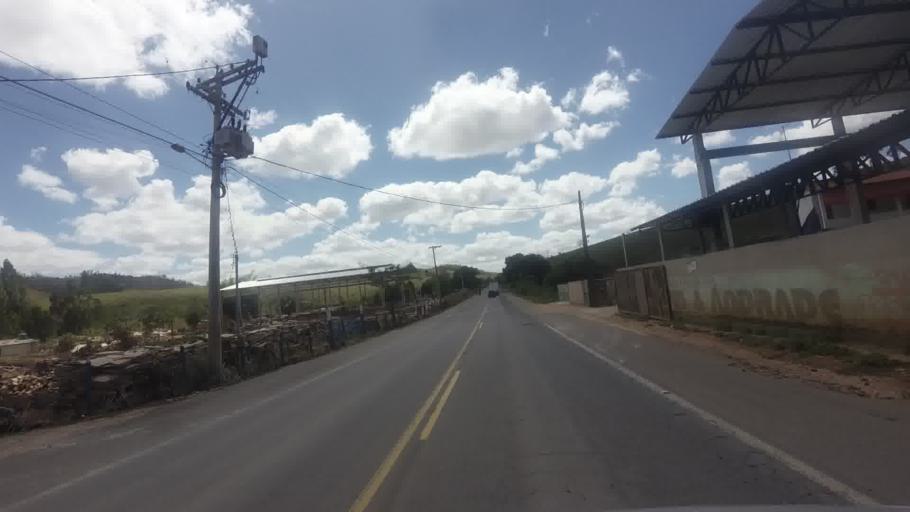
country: BR
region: Rio de Janeiro
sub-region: Santo Antonio De Padua
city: Santo Antonio de Padua
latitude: -21.6442
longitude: -42.2823
